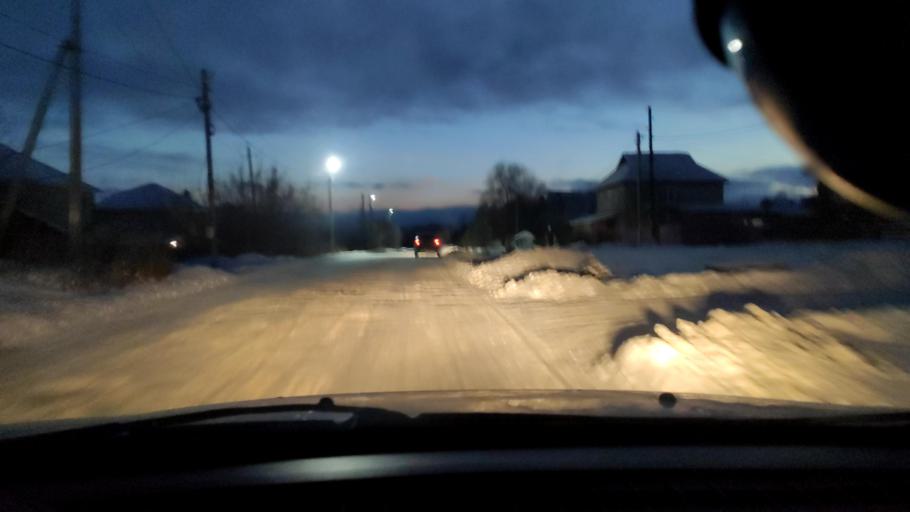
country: RU
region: Perm
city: Kultayevo
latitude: 57.9264
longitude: 55.8760
